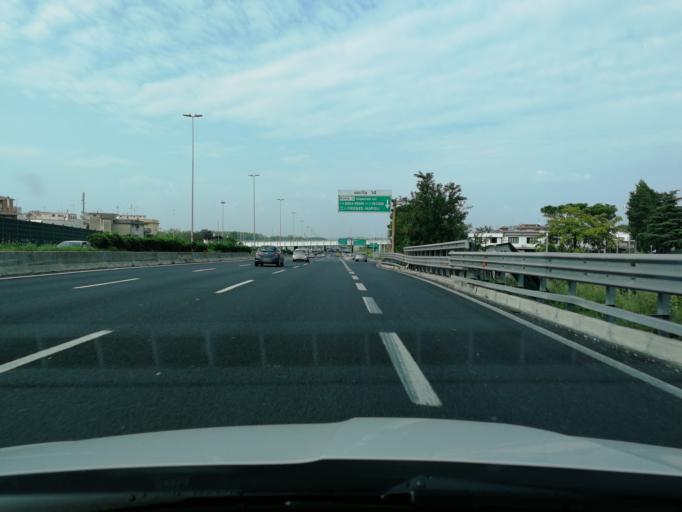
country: IT
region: Latium
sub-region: Citta metropolitana di Roma Capitale
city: Setteville
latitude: 41.9168
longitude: 12.6145
